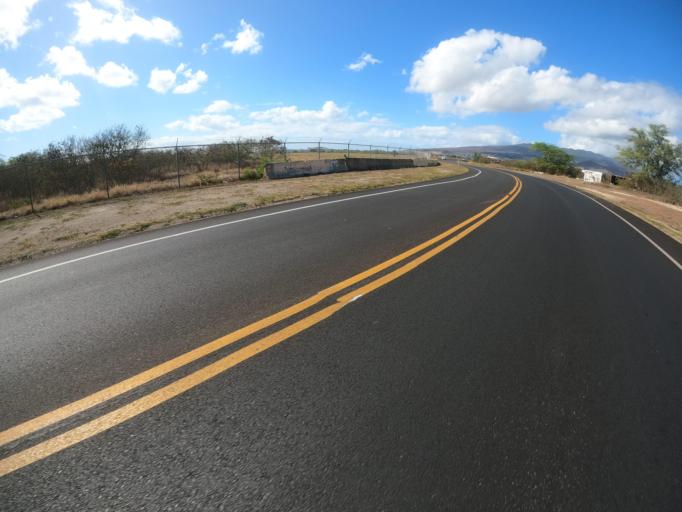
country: US
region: Hawaii
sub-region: Honolulu County
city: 'Ewa Villages
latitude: 21.3147
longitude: -158.0554
